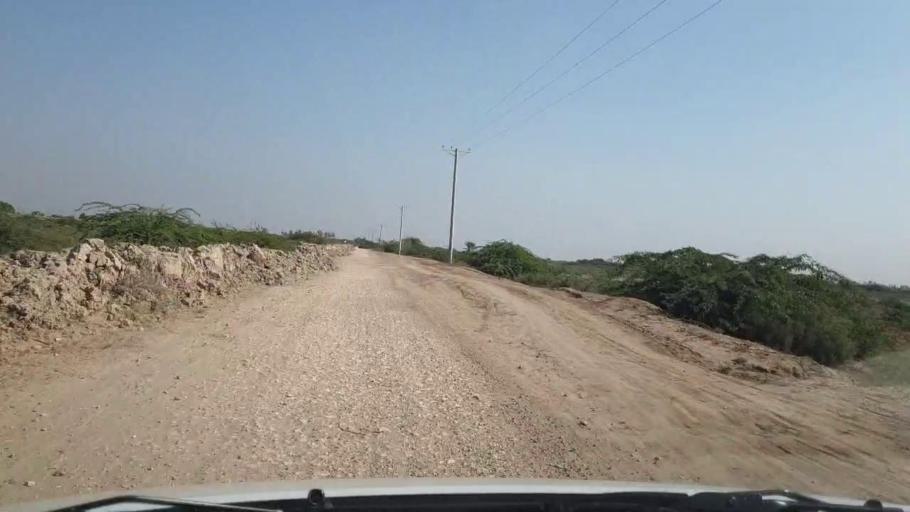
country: PK
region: Sindh
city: Mirpur Sakro
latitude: 24.6491
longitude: 67.6272
